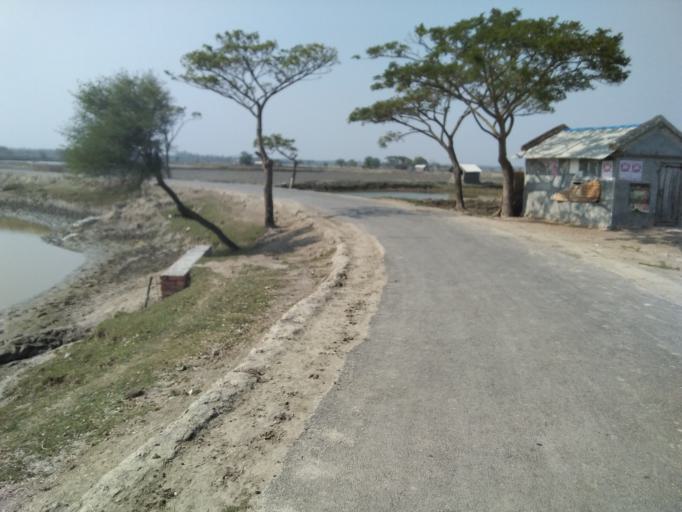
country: IN
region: West Bengal
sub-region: North 24 Parganas
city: Taki
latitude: 22.6342
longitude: 89.0131
